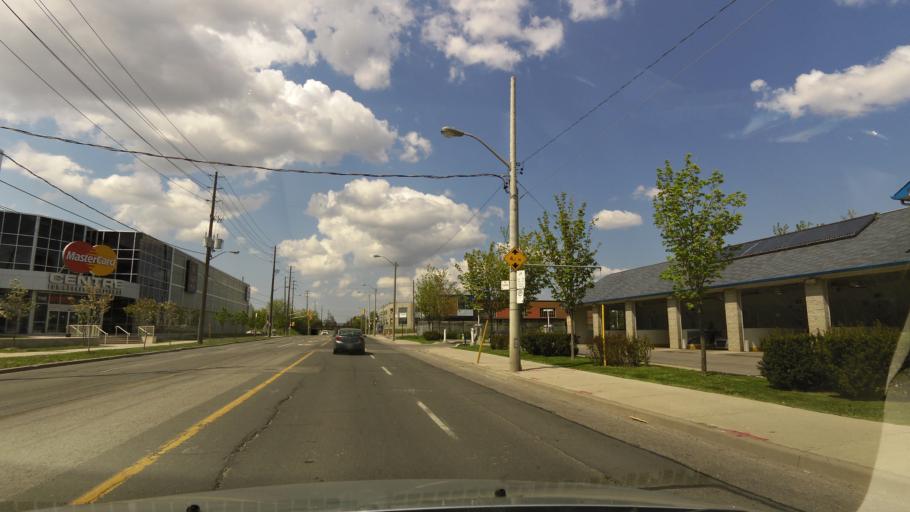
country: CA
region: Ontario
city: Etobicoke
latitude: 43.6028
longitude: -79.5189
